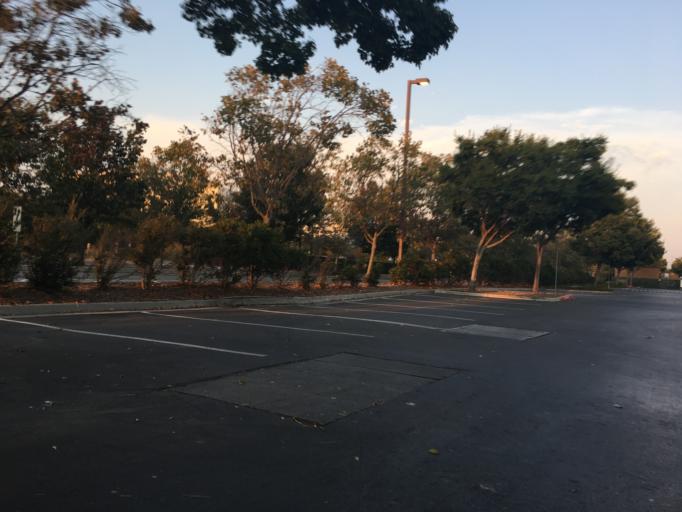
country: US
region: California
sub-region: Santa Clara County
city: Mountain View
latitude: 37.4246
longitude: -122.0739
